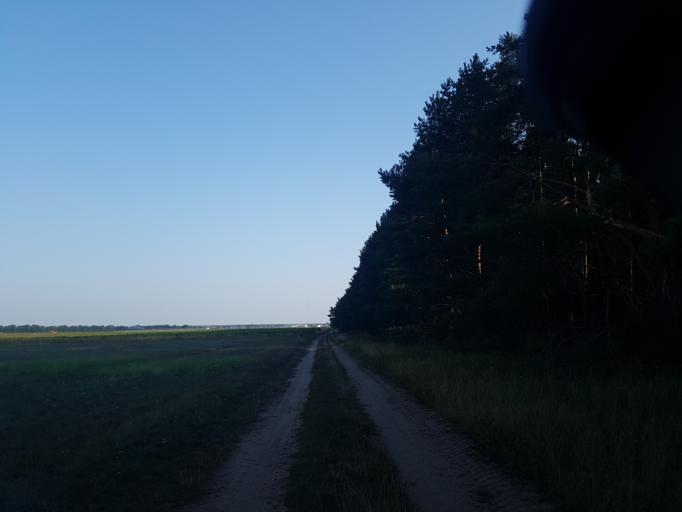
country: DE
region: Saxony-Anhalt
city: Holzdorf
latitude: 51.8353
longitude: 13.1177
